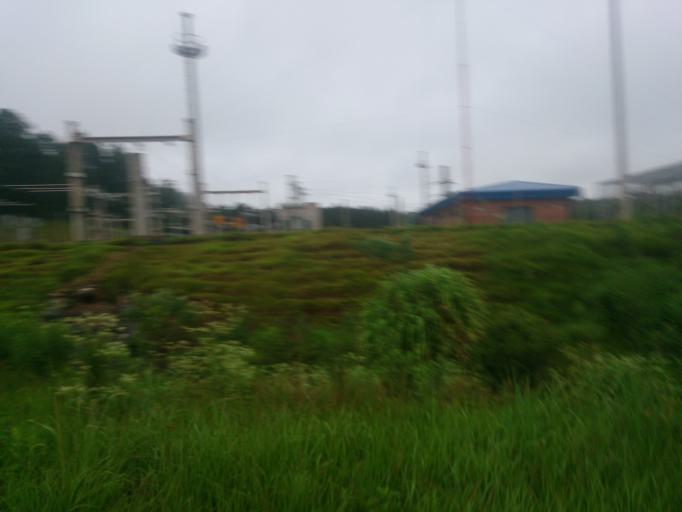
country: AR
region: Misiones
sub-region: Departamento de Obera
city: Obera
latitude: -27.4471
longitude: -55.0824
